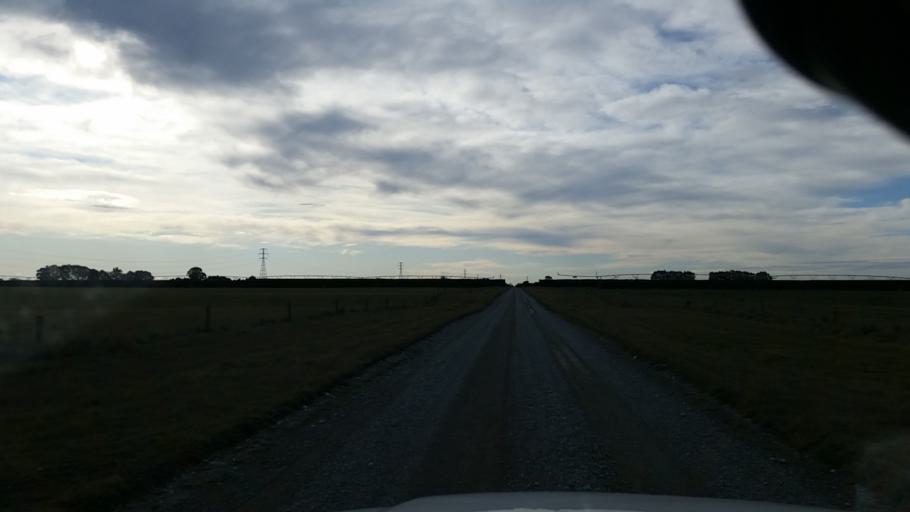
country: NZ
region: Canterbury
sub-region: Ashburton District
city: Tinwald
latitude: -44.0451
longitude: 171.4774
